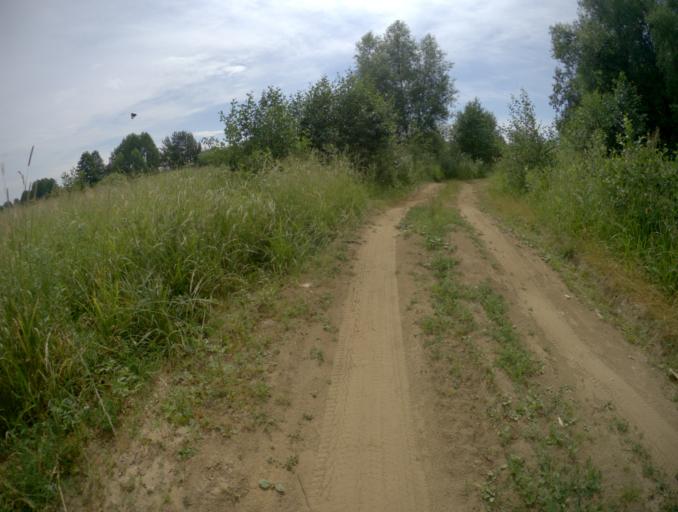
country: RU
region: Vladimir
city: Raduzhnyy
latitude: 56.0284
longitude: 40.2885
